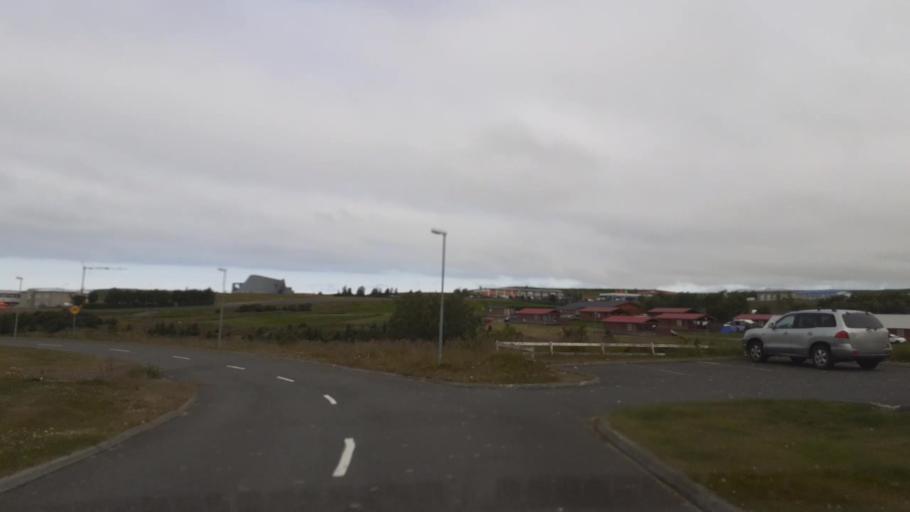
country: IS
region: Northwest
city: Saudarkrokur
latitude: 65.6565
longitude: -20.2783
